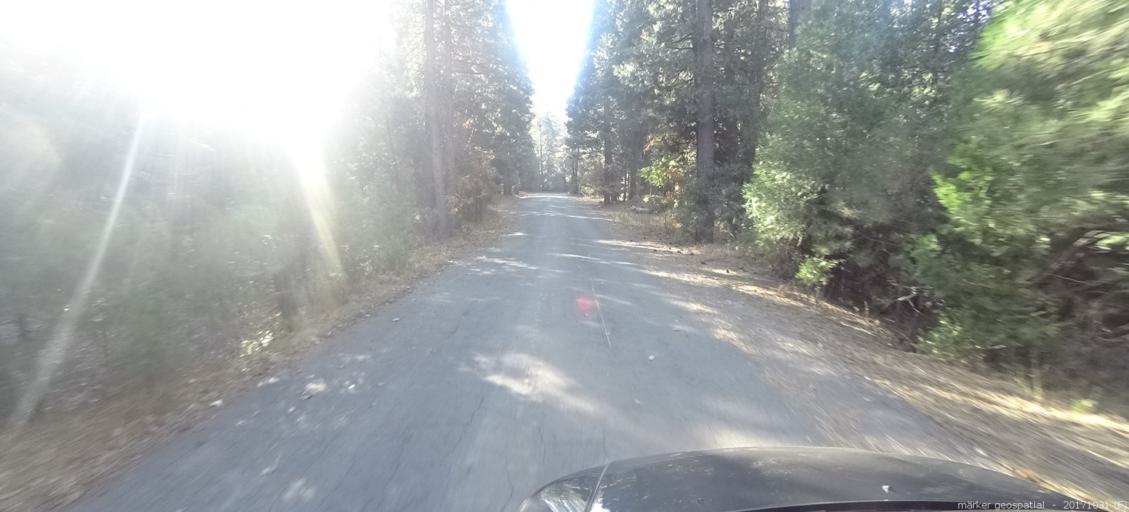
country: US
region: California
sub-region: Shasta County
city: Shingletown
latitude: 40.5285
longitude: -121.8359
